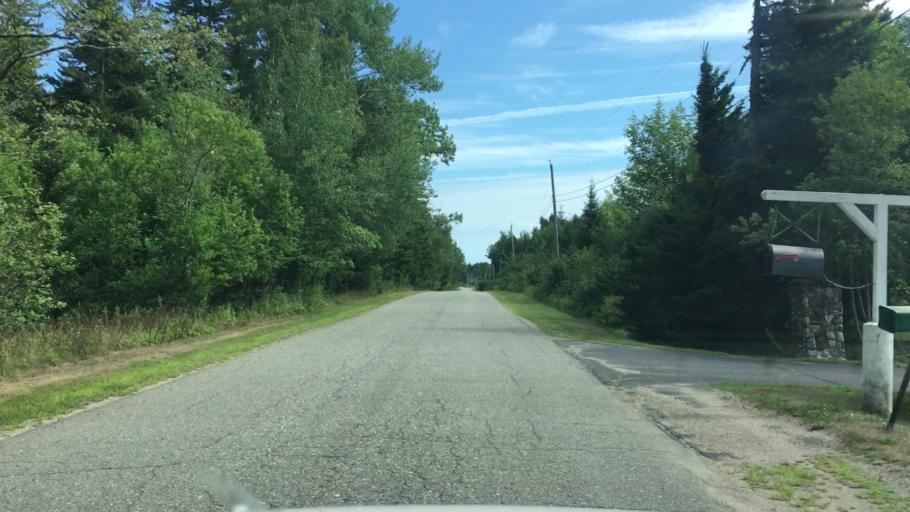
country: US
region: Maine
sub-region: Washington County
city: Eastport
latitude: 44.9324
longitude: -67.0434
